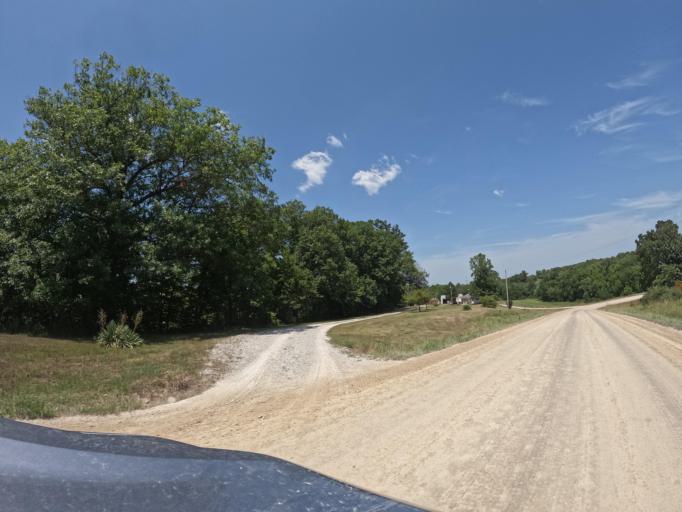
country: US
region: Iowa
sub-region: Henry County
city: Mount Pleasant
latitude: 40.9562
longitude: -91.5955
